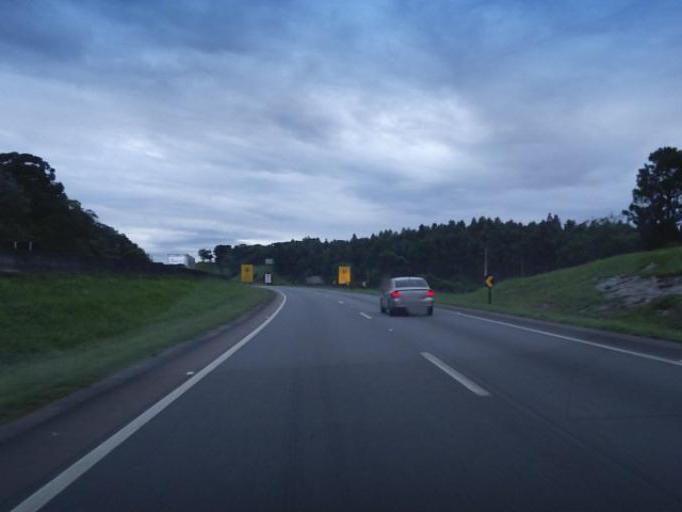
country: BR
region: Parana
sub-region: Sao Jose Dos Pinhais
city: Sao Jose dos Pinhais
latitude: -25.8069
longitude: -49.1350
